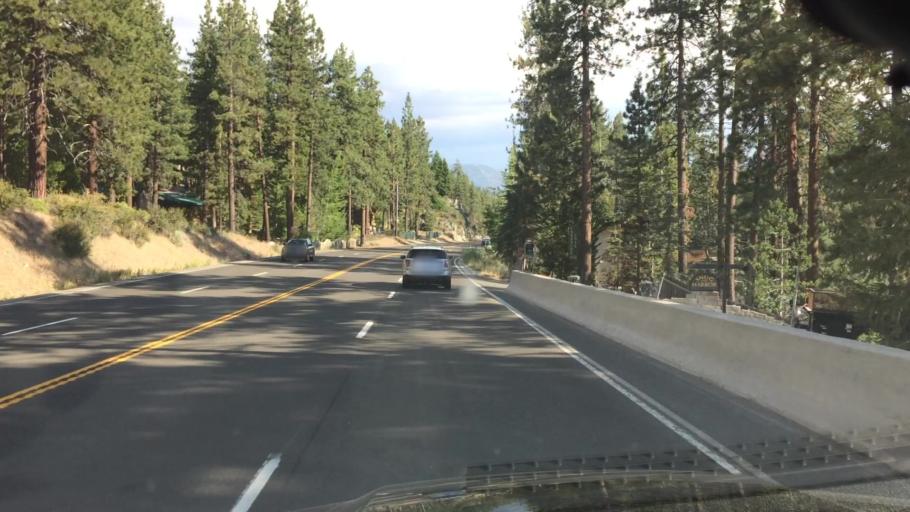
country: US
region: Nevada
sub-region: Douglas County
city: Kingsbury
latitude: 39.0311
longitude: -119.9468
